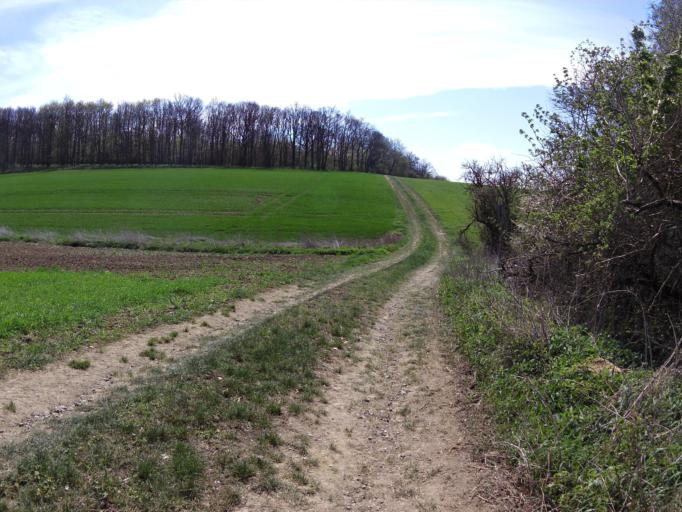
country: DE
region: Bavaria
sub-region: Regierungsbezirk Unterfranken
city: Rottendorf
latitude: 49.7844
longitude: 10.0534
